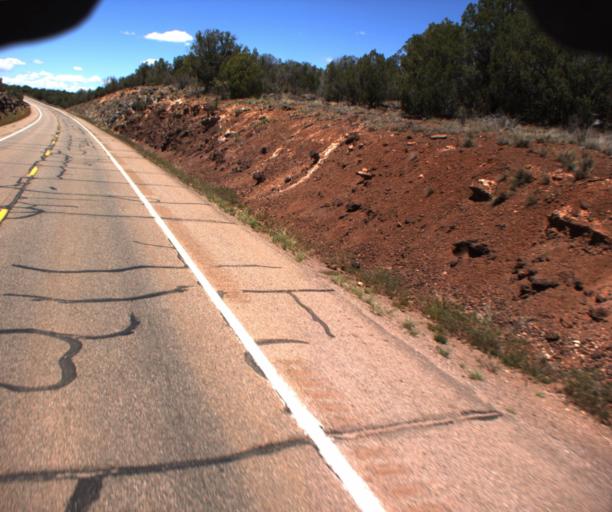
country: US
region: Arizona
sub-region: Yavapai County
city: Paulden
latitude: 35.0824
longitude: -112.4059
